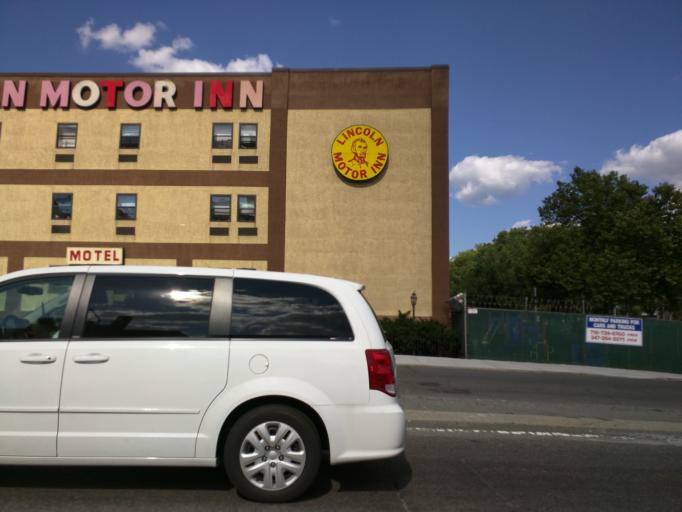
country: US
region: New York
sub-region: Queens County
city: Jamaica
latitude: 40.6997
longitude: -73.8148
